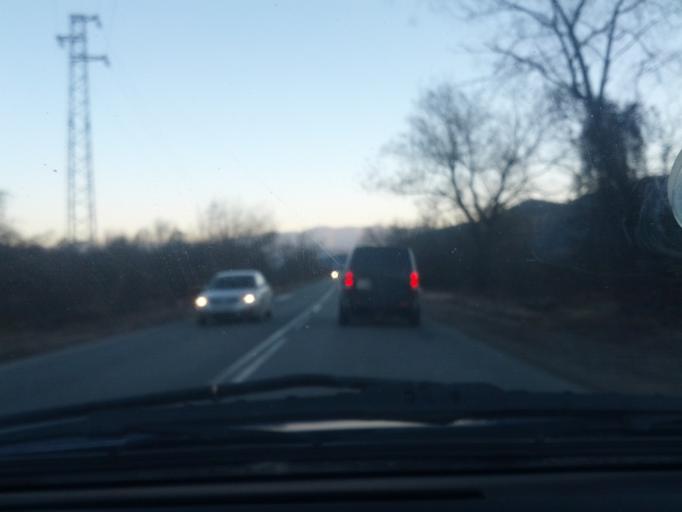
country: BG
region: Sofiya
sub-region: Obshtina Botevgrad
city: Botevgrad
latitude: 43.0072
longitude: 23.7016
